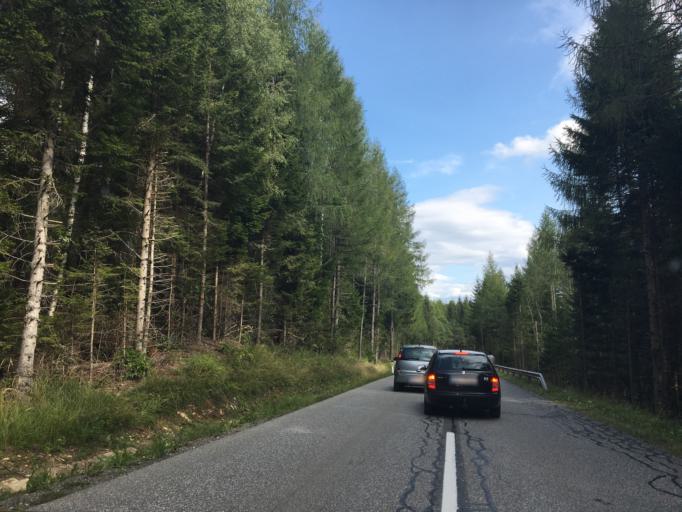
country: AT
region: Styria
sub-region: Politischer Bezirk Deutschlandsberg
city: Kloster
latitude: 46.8298
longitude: 15.0662
